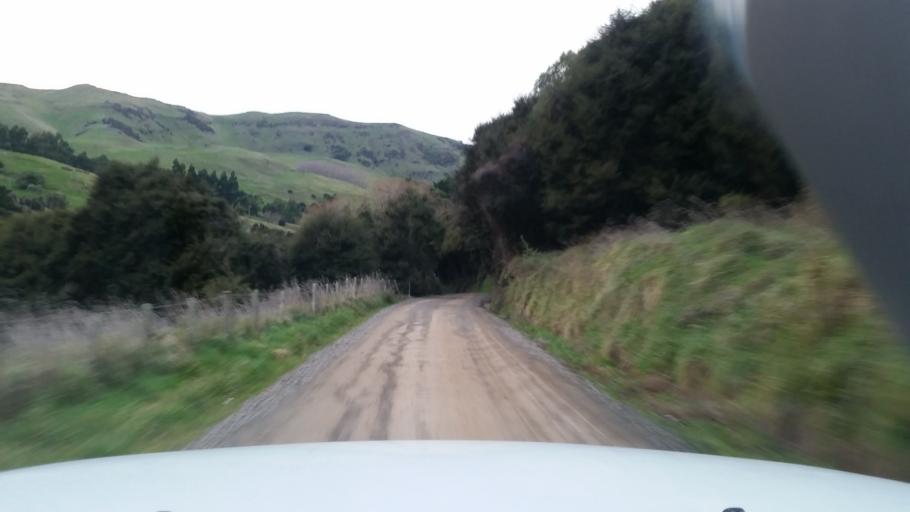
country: NZ
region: Canterbury
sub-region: Christchurch City
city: Christchurch
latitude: -43.7367
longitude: 172.7895
